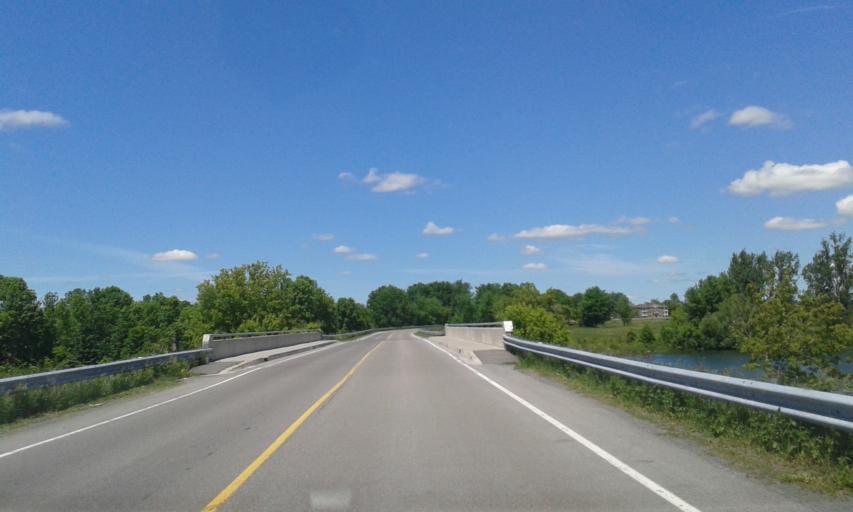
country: US
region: New York
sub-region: St. Lawrence County
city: Massena
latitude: 45.0233
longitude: -74.8948
